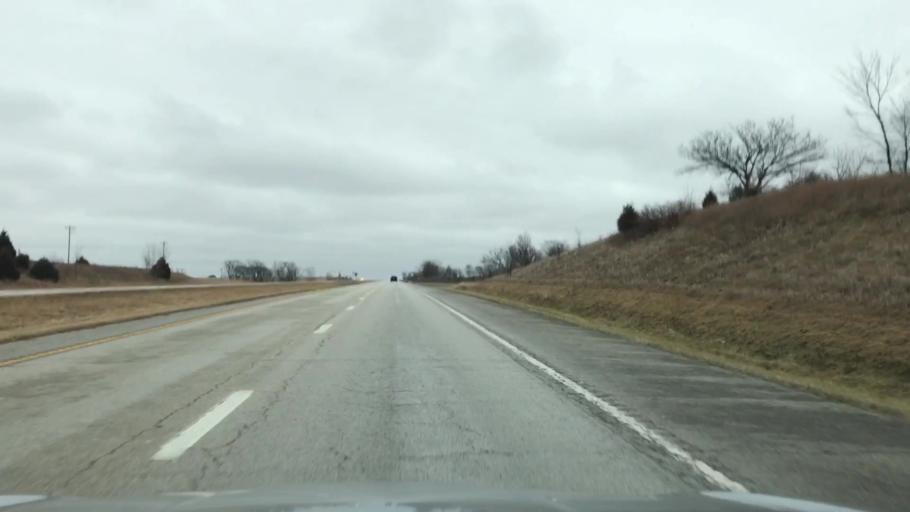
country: US
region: Missouri
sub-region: Clinton County
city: Cameron
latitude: 39.7511
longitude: -94.1515
